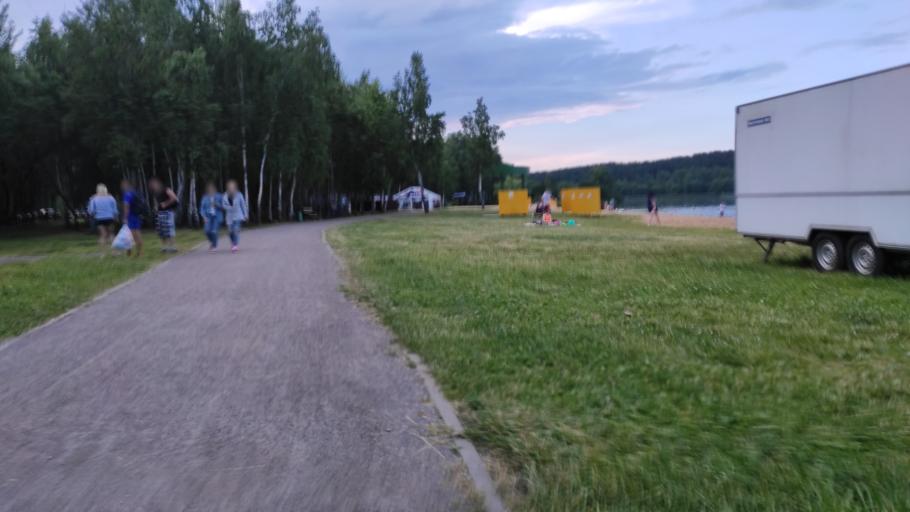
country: BY
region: Minsk
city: Zhdanovichy
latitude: 53.9589
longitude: 27.4454
